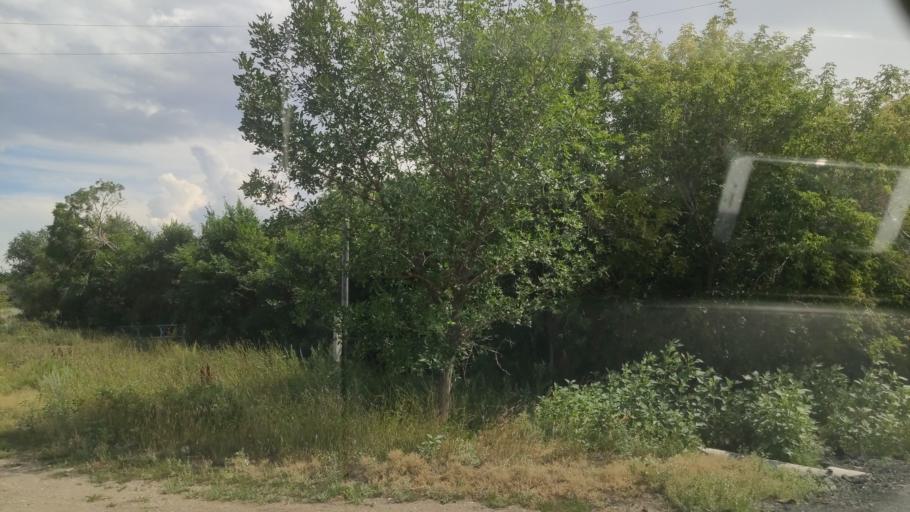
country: KZ
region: Pavlodar
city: Pavlodar
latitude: 52.6177
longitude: 77.2076
